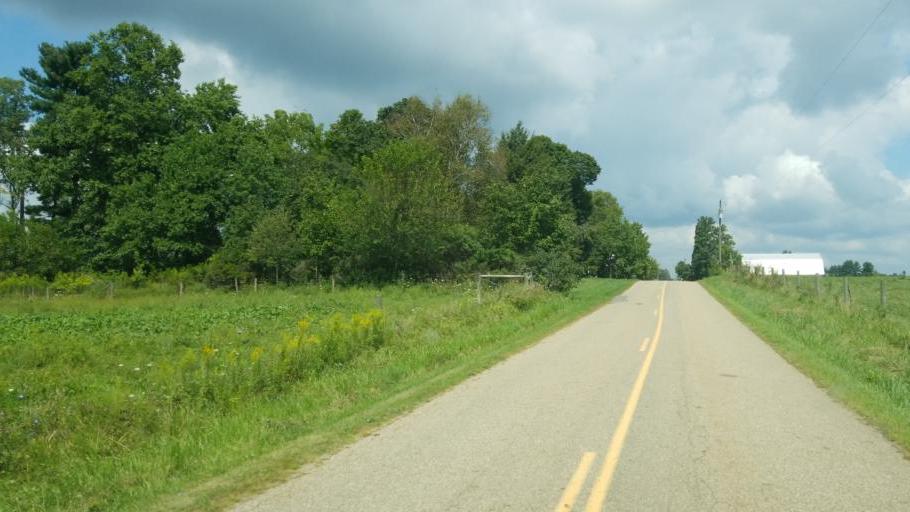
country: US
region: Ohio
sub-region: Licking County
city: Utica
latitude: 40.2831
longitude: -82.4900
